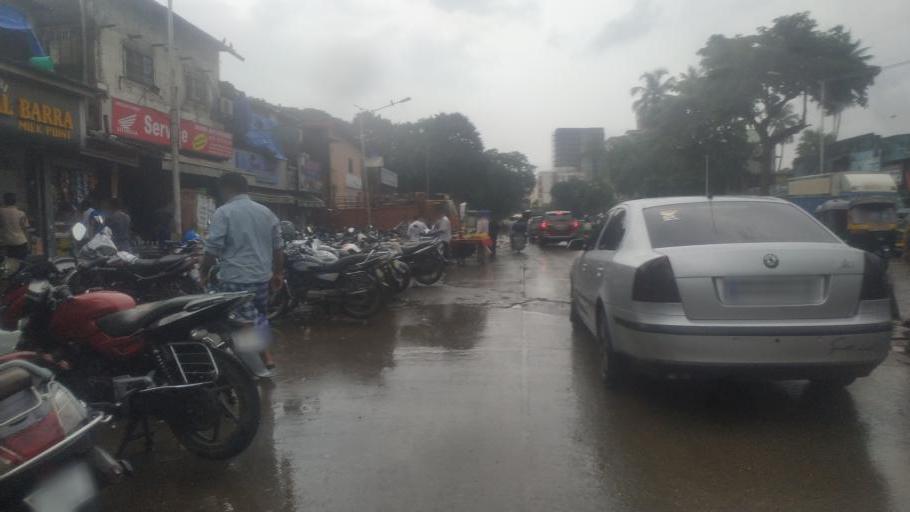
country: IN
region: Maharashtra
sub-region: Mumbai Suburban
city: Mumbai
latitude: 19.0625
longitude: 72.8733
